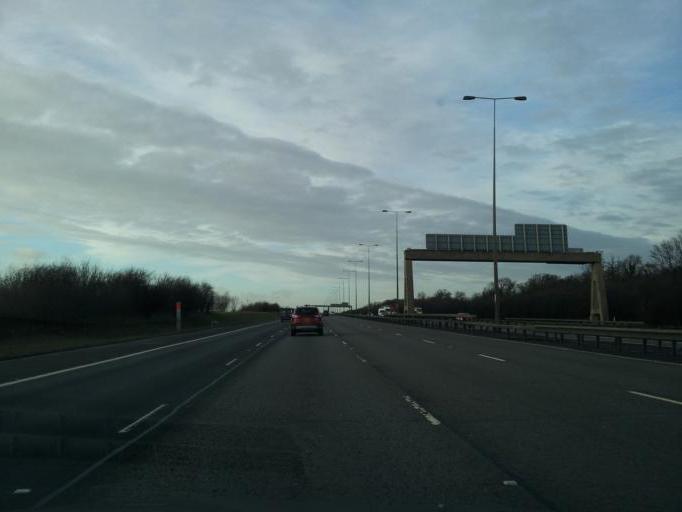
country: GB
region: England
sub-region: Cambridgeshire
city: Sawtry
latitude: 52.4513
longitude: -0.2787
